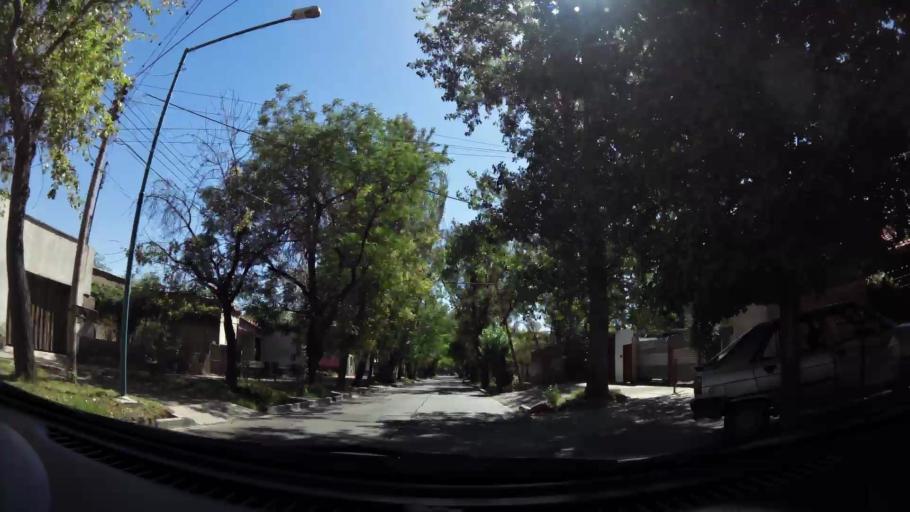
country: AR
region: Mendoza
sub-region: Departamento de Godoy Cruz
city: Godoy Cruz
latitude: -32.9493
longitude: -68.8404
